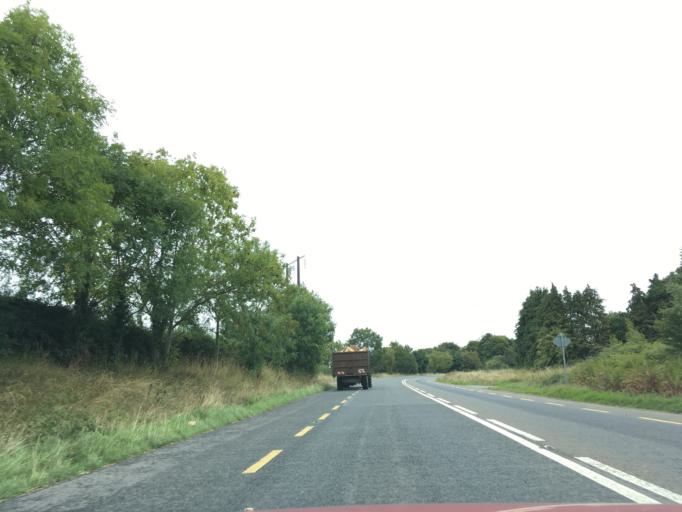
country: IE
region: Munster
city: Carrick-on-Suir
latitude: 52.3656
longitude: -7.5502
